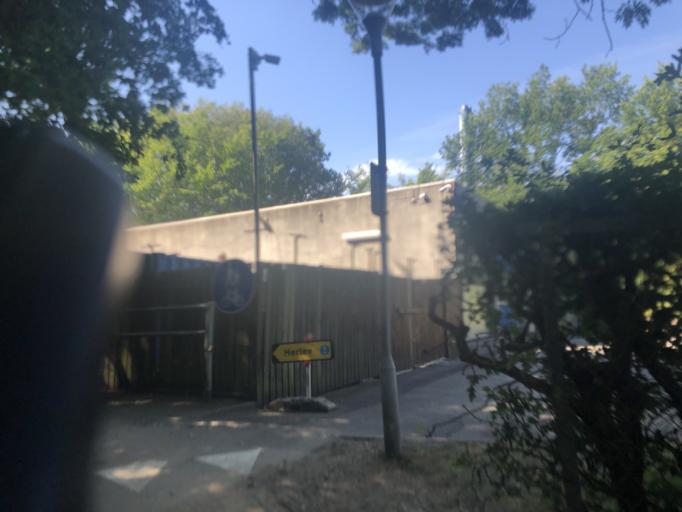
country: DK
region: Capital Region
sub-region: Herlev Kommune
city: Herlev
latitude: 55.7371
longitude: 12.4654
